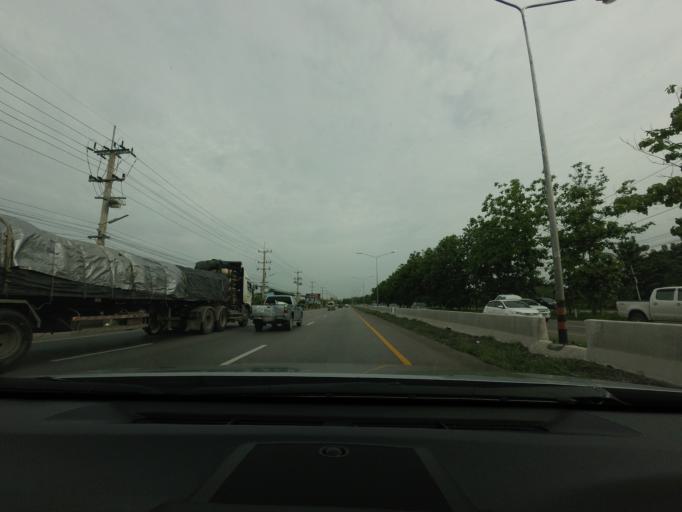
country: TH
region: Phetchaburi
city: Phetchaburi
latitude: 13.1411
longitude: 99.8581
